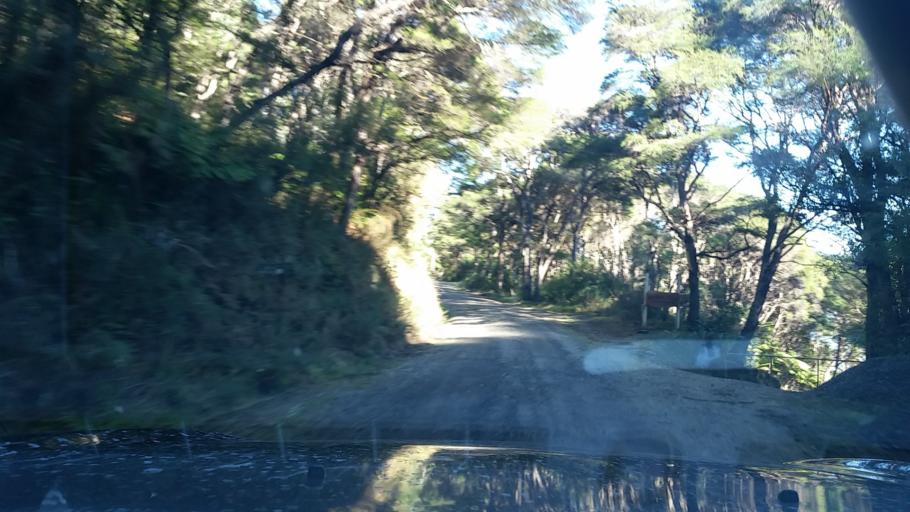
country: NZ
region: Marlborough
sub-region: Marlborough District
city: Picton
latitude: -41.1810
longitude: 173.9750
